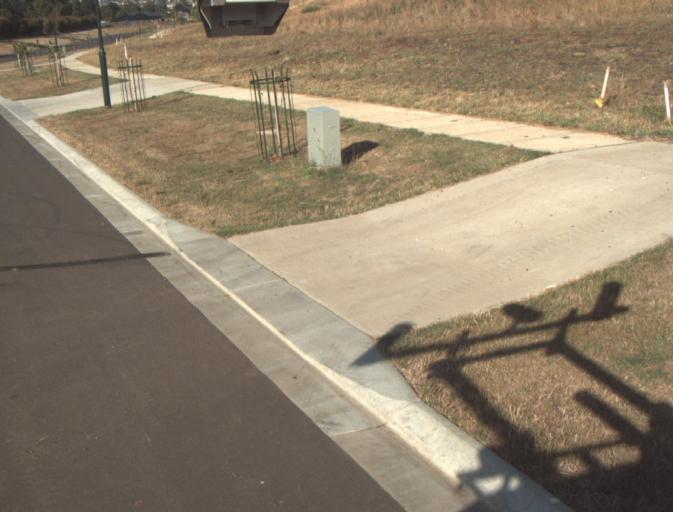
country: AU
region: Tasmania
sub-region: Launceston
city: Invermay
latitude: -41.3919
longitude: 147.1380
